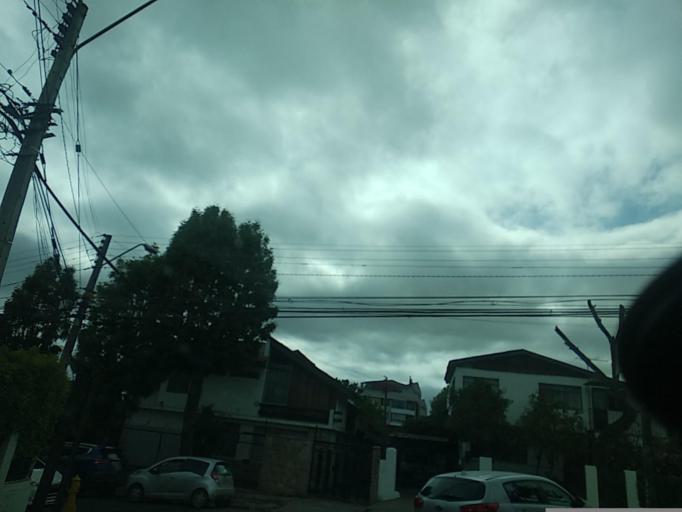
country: CL
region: Valparaiso
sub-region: Provincia de Marga Marga
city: Quilpue
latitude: -33.0485
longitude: -71.4478
